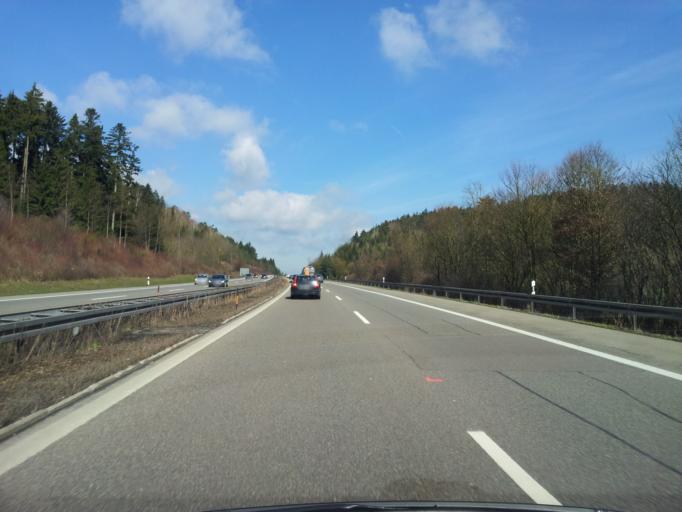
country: DE
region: Baden-Wuerttemberg
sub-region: Freiburg Region
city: Vohringen
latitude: 48.2866
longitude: 8.6401
